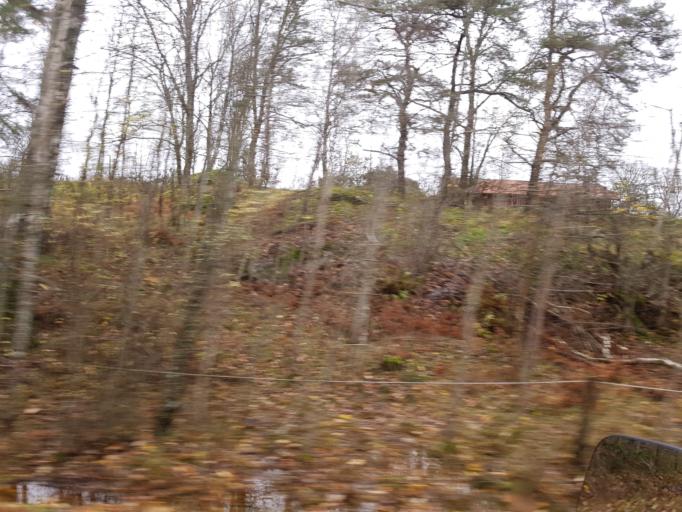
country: SE
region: Vaestra Goetaland
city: Svanesund
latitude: 58.2103
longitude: 11.7723
